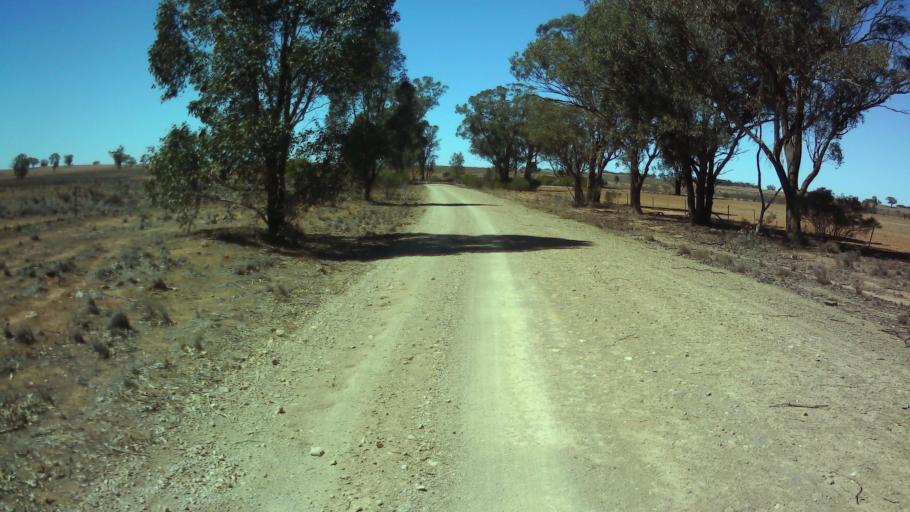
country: AU
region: New South Wales
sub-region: Forbes
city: Forbes
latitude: -33.6980
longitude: 147.8675
